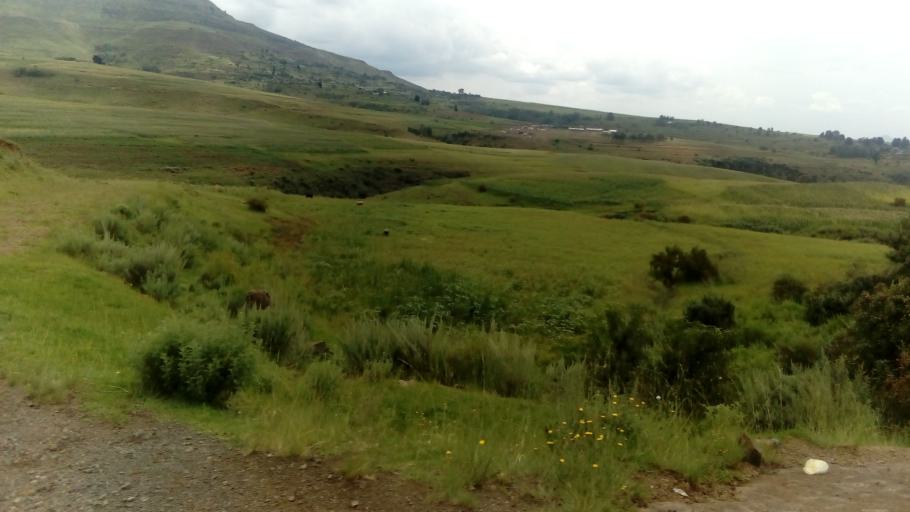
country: LS
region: Leribe
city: Leribe
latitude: -29.0365
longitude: 28.2524
